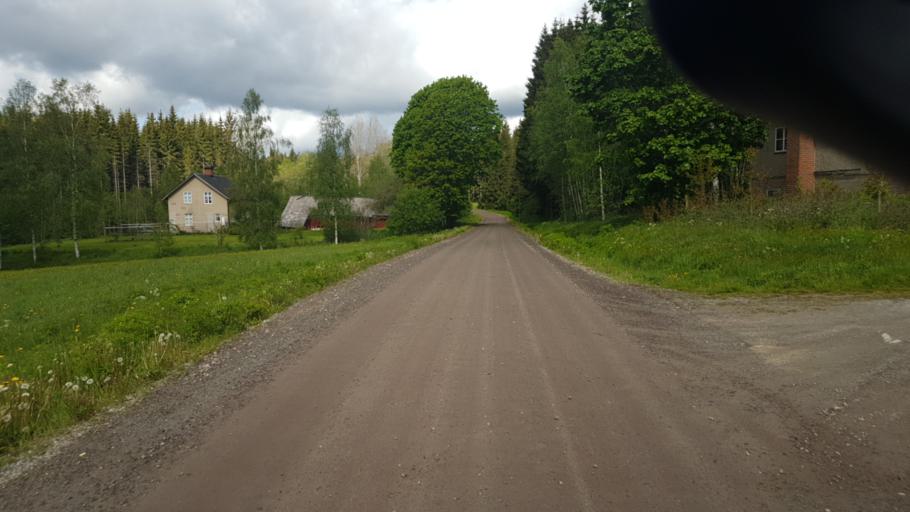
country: NO
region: Ostfold
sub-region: Romskog
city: Romskog
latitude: 59.7001
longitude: 12.0636
